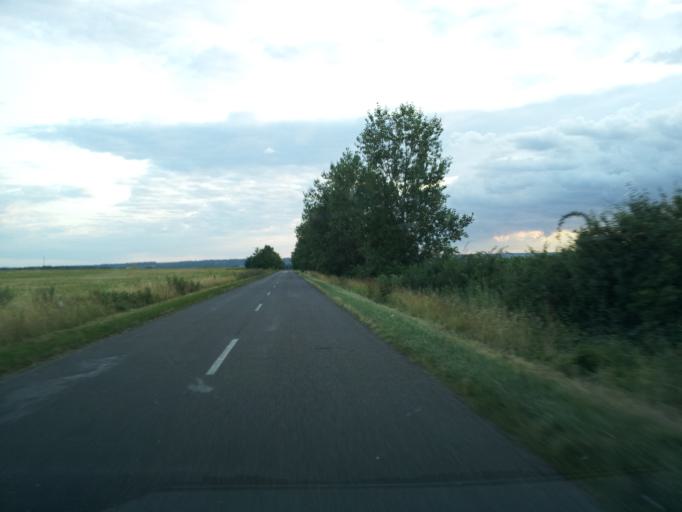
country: HU
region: Somogy
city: Adand
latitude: 46.8092
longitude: 18.1866
